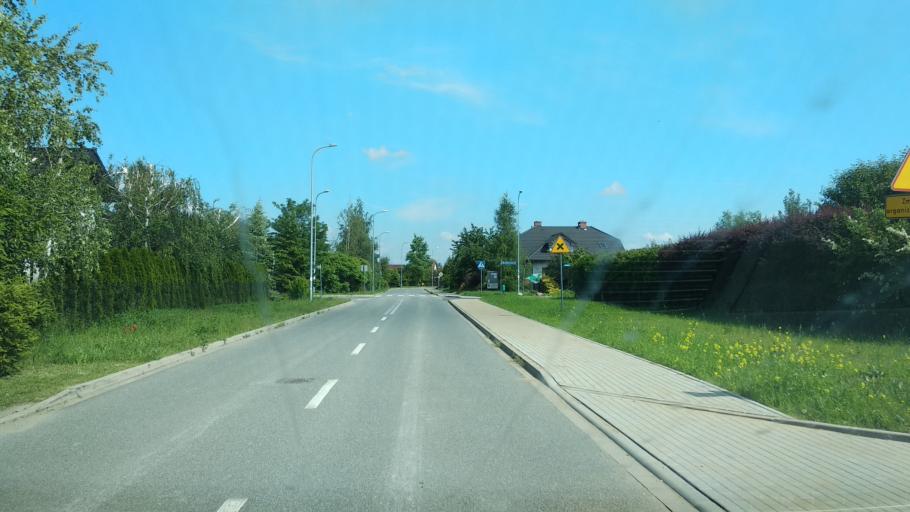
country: PL
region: Lower Silesian Voivodeship
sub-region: Powiat wroclawski
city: Zorawina
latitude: 50.9843
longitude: 17.0410
